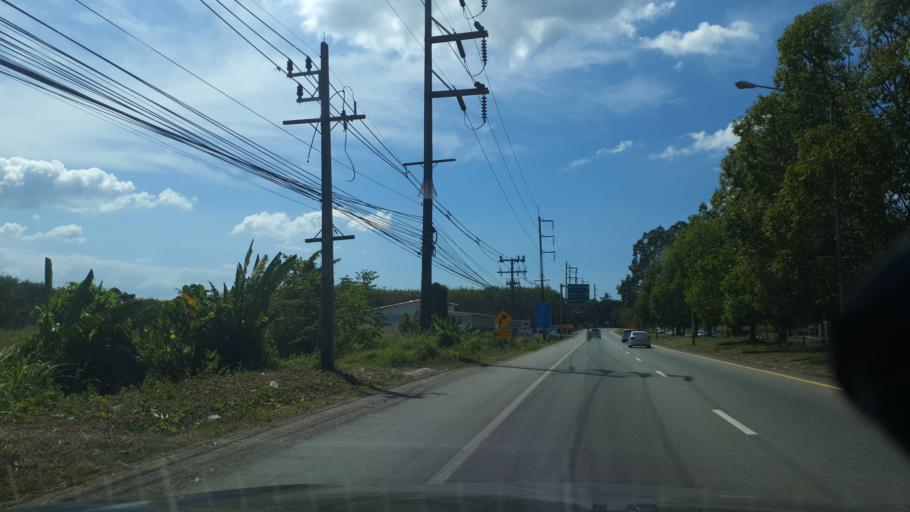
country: TH
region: Phangnga
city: Thai Mueang
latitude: 8.2717
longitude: 98.3425
